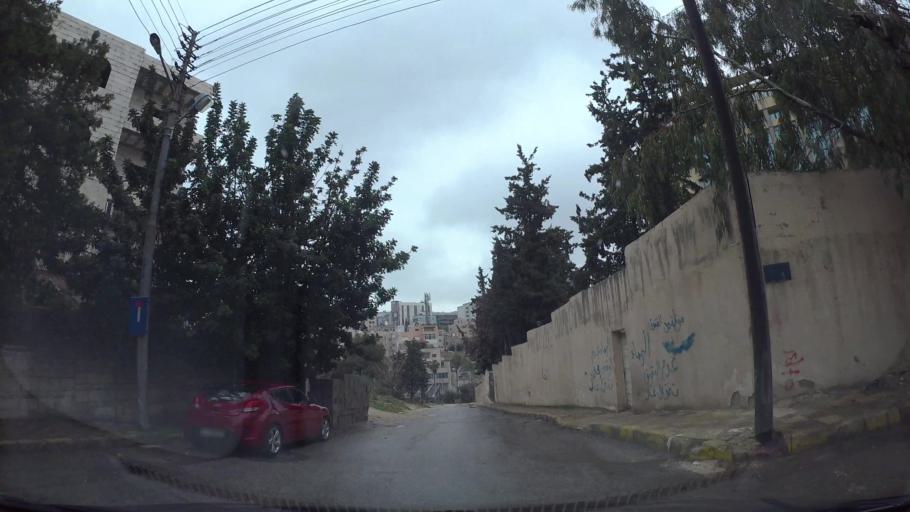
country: JO
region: Amman
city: Amman
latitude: 31.9606
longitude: 35.9031
